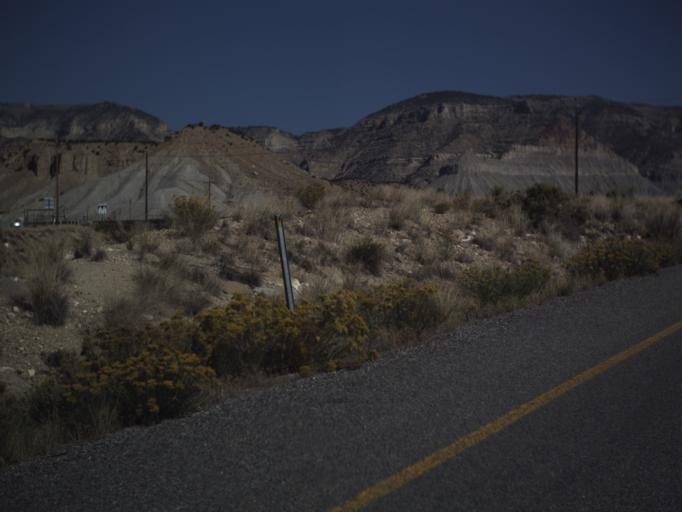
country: US
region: Utah
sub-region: Emery County
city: Orangeville
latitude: 39.2535
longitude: -111.0974
